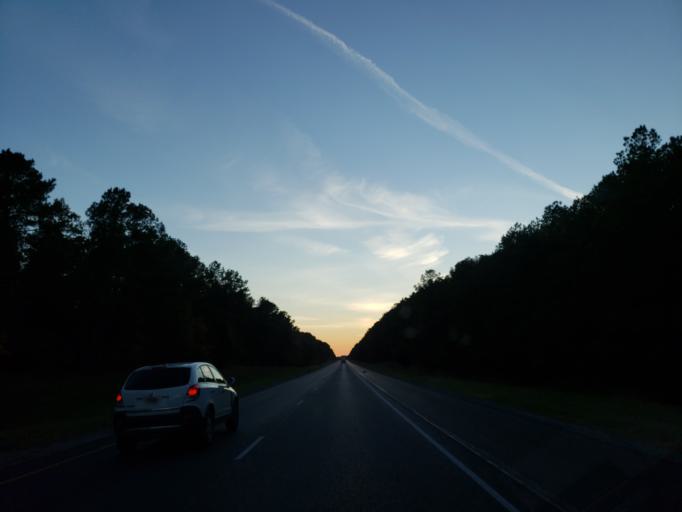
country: US
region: Alabama
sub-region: Sumter County
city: Livingston
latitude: 32.5790
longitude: -88.2377
